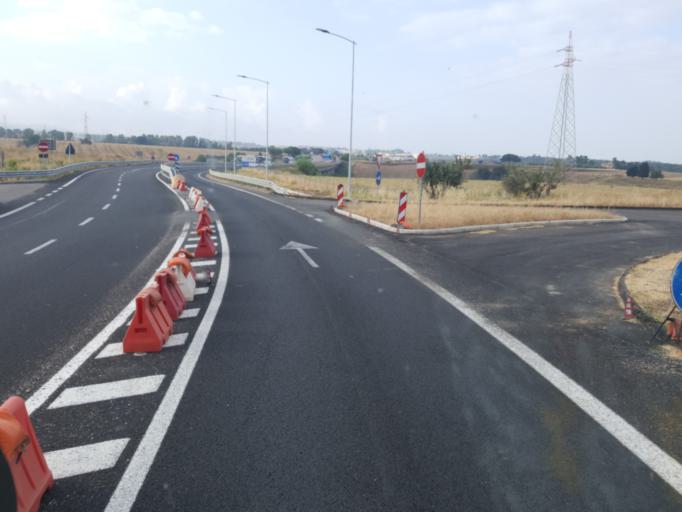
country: IT
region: Latium
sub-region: Citta metropolitana di Roma Capitale
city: Aurelia
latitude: 42.1631
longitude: 11.7879
